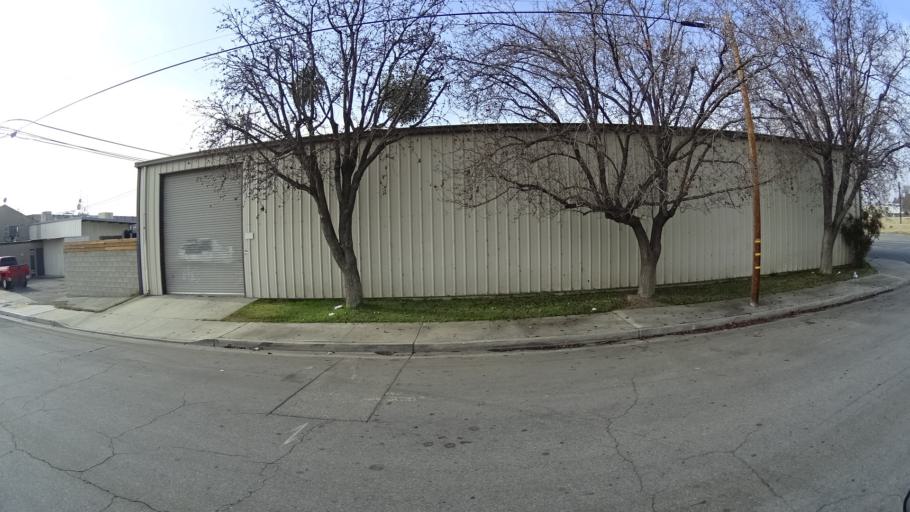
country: US
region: California
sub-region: Kern County
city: Bakersfield
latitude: 35.3787
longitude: -119.0048
